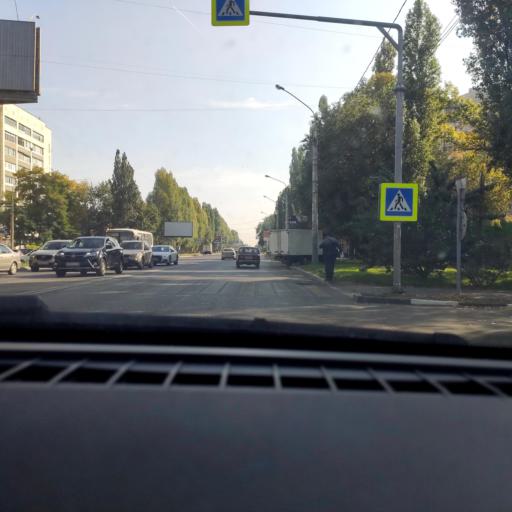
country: RU
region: Voronezj
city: Voronezh
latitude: 51.6710
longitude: 39.2562
